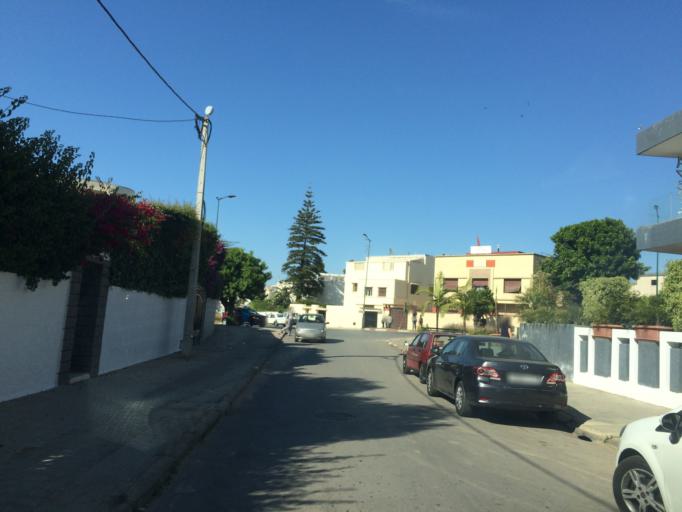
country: MA
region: Rabat-Sale-Zemmour-Zaer
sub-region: Rabat
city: Rabat
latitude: 33.9912
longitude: -6.8185
